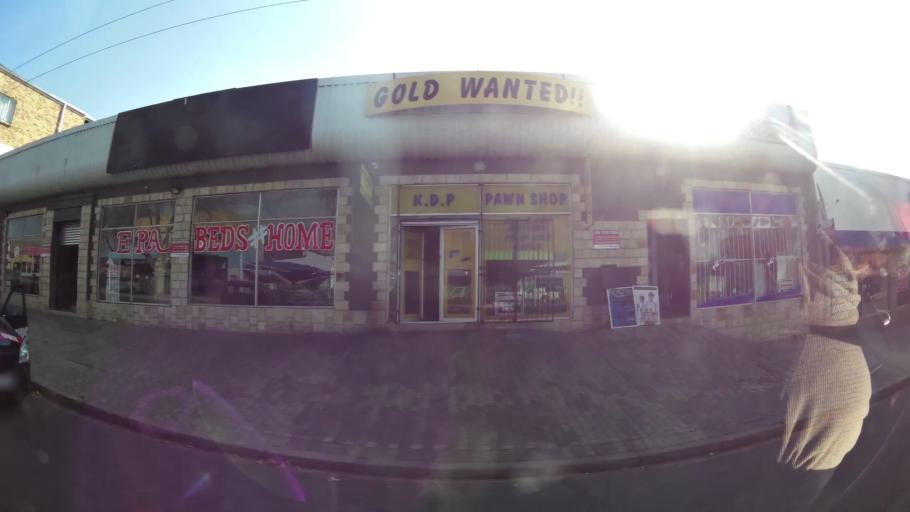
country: ZA
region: Gauteng
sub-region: West Rand District Municipality
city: Krugersdorp
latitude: -26.0993
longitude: 27.7743
